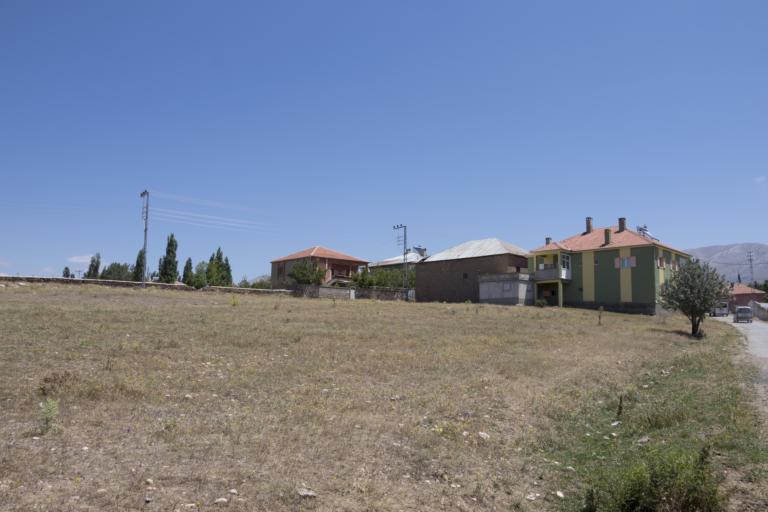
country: TR
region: Kayseri
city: Toklar
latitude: 38.4066
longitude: 36.0768
